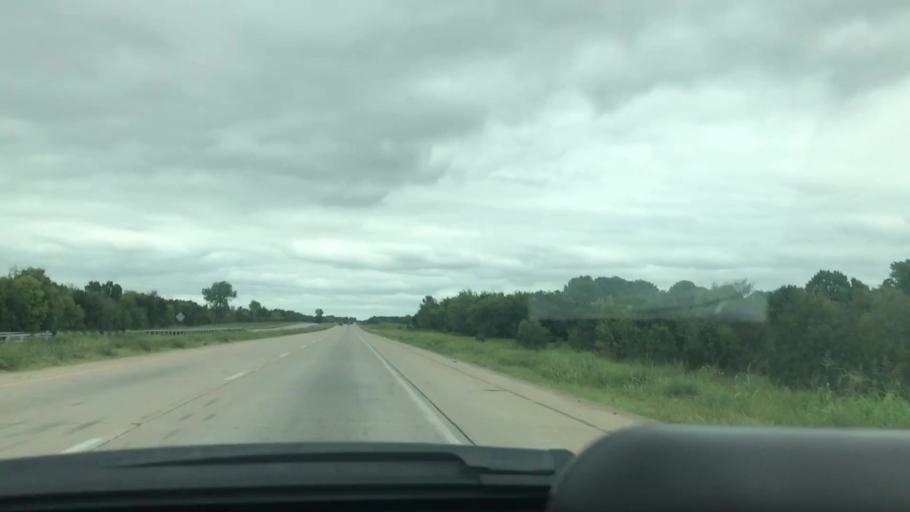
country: US
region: Oklahoma
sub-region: Mayes County
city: Chouteau
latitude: 36.2074
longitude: -95.3408
